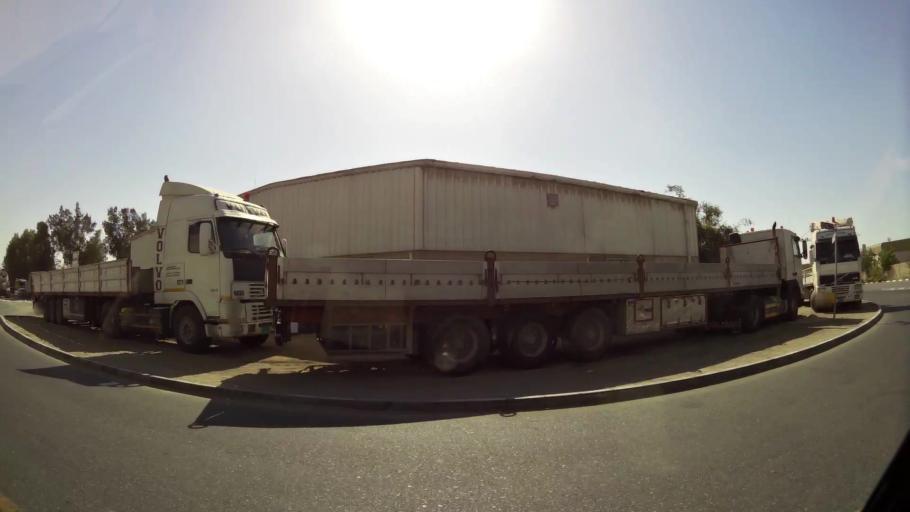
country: AE
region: Dubai
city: Dubai
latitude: 25.1194
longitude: 55.2215
